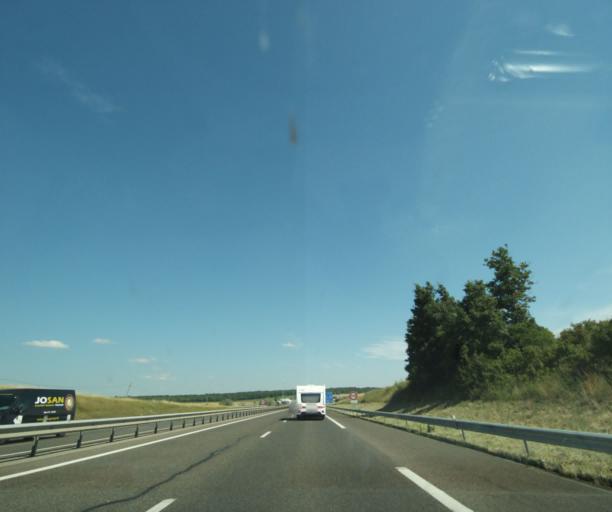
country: FR
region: Lorraine
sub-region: Departement de Meurthe-et-Moselle
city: Blenod-les-Toul
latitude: 48.6228
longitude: 5.8855
